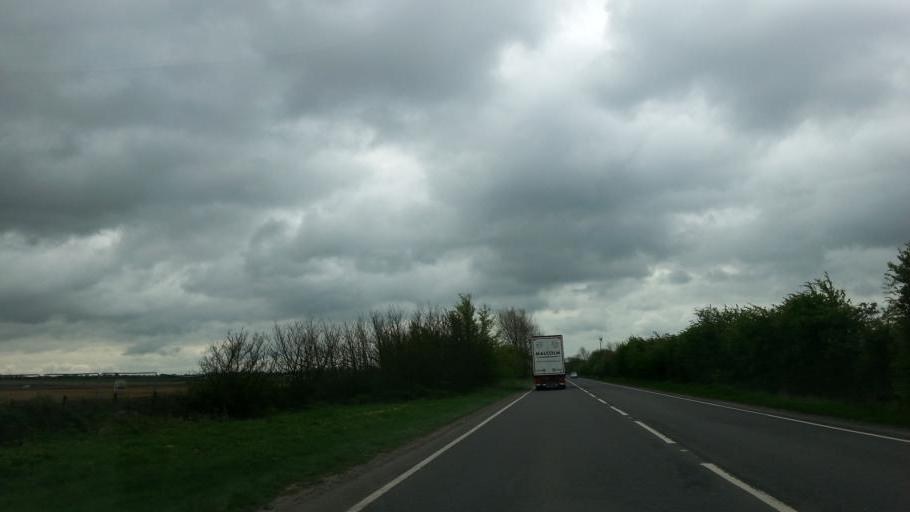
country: GB
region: England
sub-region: Warwickshire
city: Rugby
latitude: 52.3695
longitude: -1.1791
